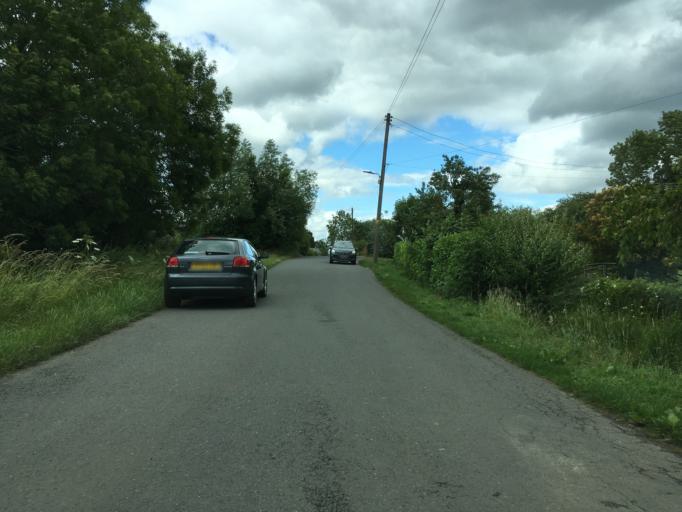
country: GB
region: England
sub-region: Gloucestershire
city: Stonehouse
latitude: 51.7879
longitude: -2.3632
